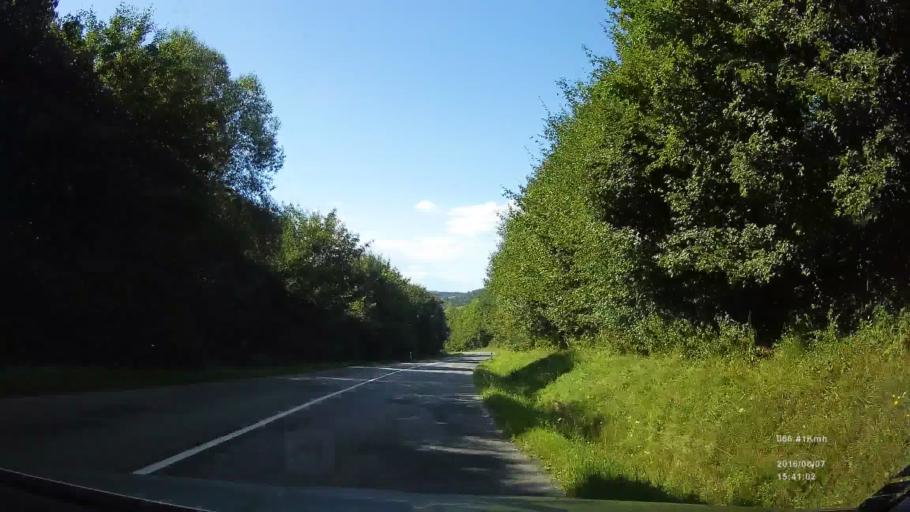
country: SK
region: Presovsky
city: Giraltovce
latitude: 49.1220
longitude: 21.5829
